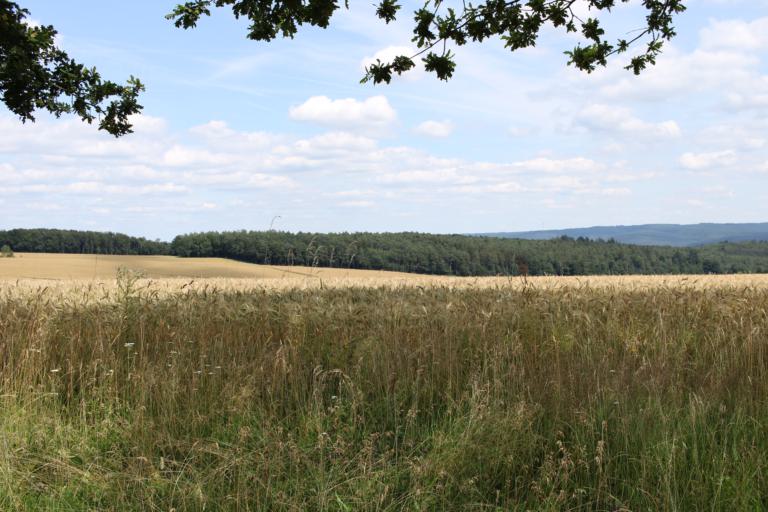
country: DE
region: Hesse
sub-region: Regierungsbezirk Darmstadt
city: Erbach
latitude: 49.6662
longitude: 8.9380
